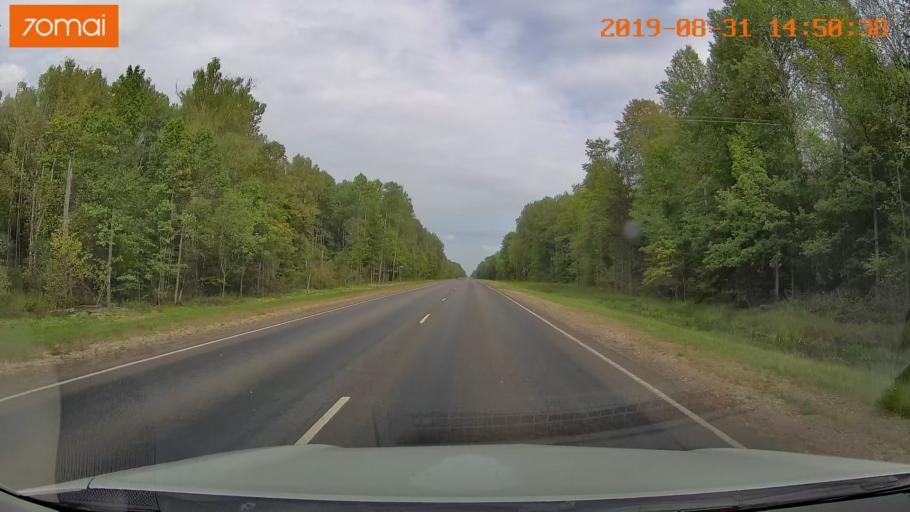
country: RU
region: Kaluga
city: Spas-Demensk
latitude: 54.2629
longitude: 33.7949
